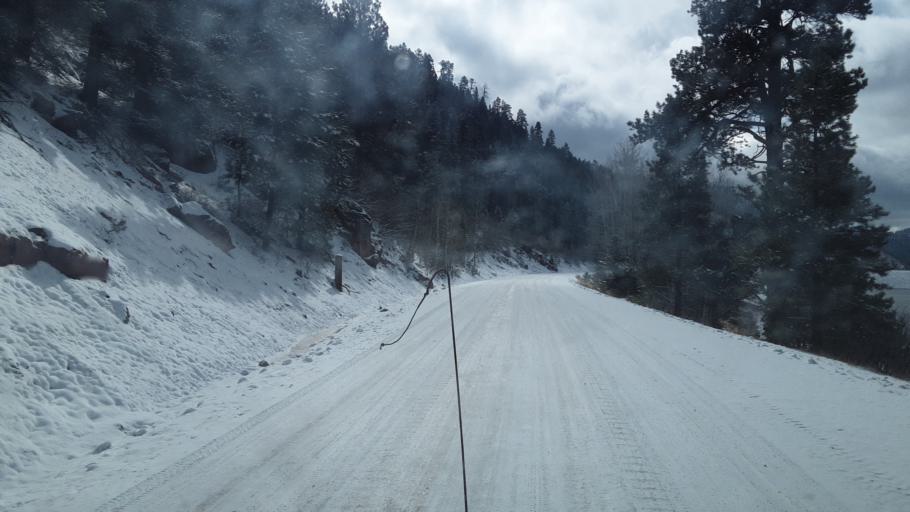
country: US
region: Colorado
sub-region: La Plata County
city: Bayfield
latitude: 37.3931
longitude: -107.6571
